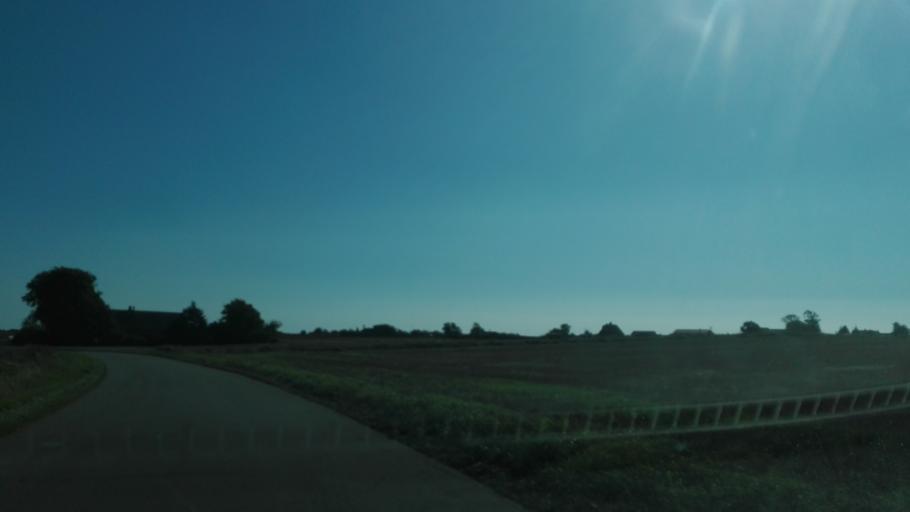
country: DK
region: Central Jutland
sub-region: Syddjurs Kommune
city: Ebeltoft
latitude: 56.2201
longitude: 10.7248
